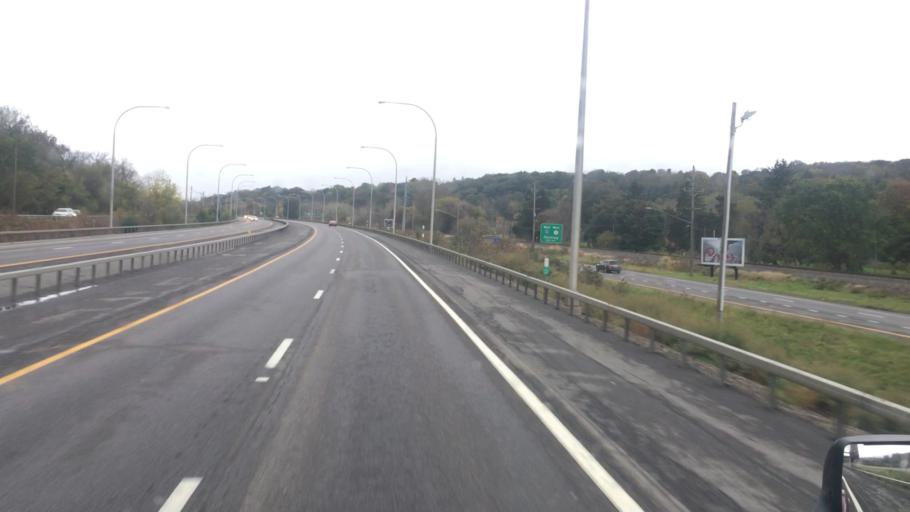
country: US
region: New York
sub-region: Broome County
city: Endwell
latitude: 42.1166
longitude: -75.9953
